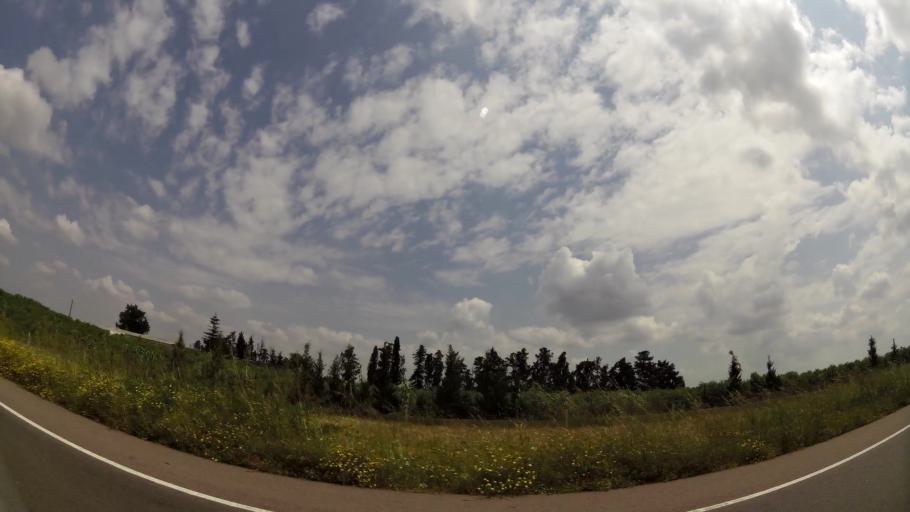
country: MA
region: Rabat-Sale-Zemmour-Zaer
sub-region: Khemisset
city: Tiflet
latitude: 33.9841
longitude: -6.5318
